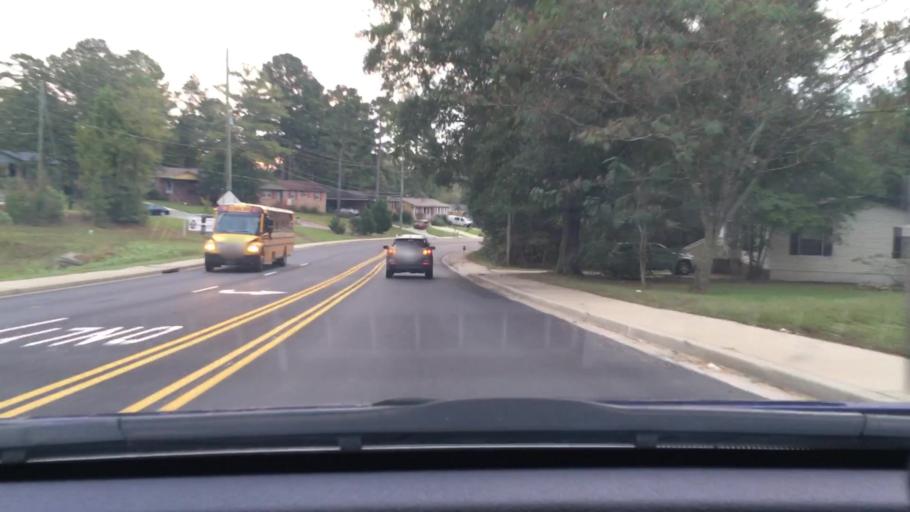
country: US
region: South Carolina
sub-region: Lexington County
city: Irmo
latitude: 34.1139
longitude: -81.1643
